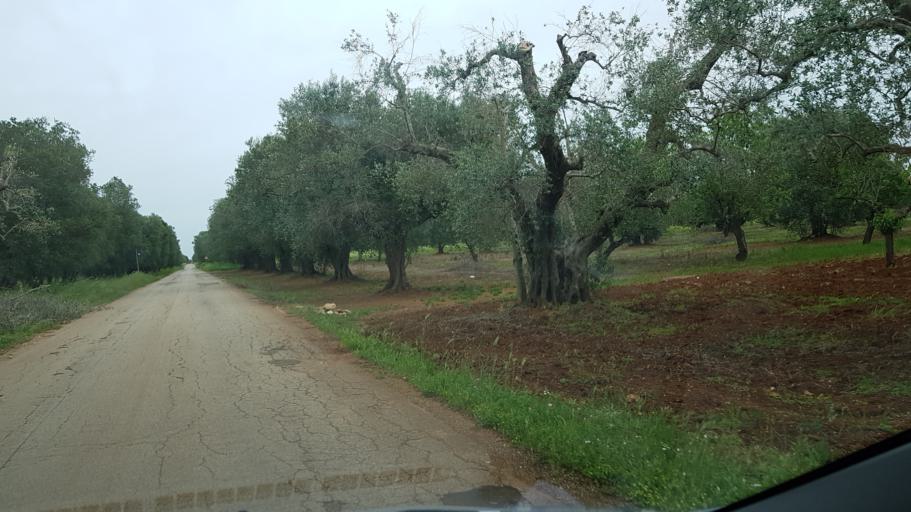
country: IT
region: Apulia
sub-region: Provincia di Brindisi
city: San Vito dei Normanni
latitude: 40.6221
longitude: 17.7589
